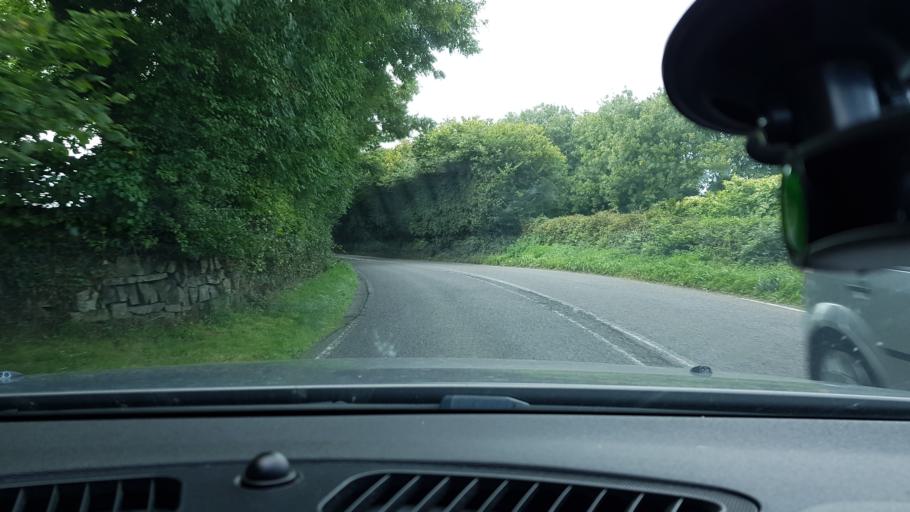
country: GB
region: England
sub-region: Cornwall
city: Camelford
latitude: 50.5970
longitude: -4.7128
